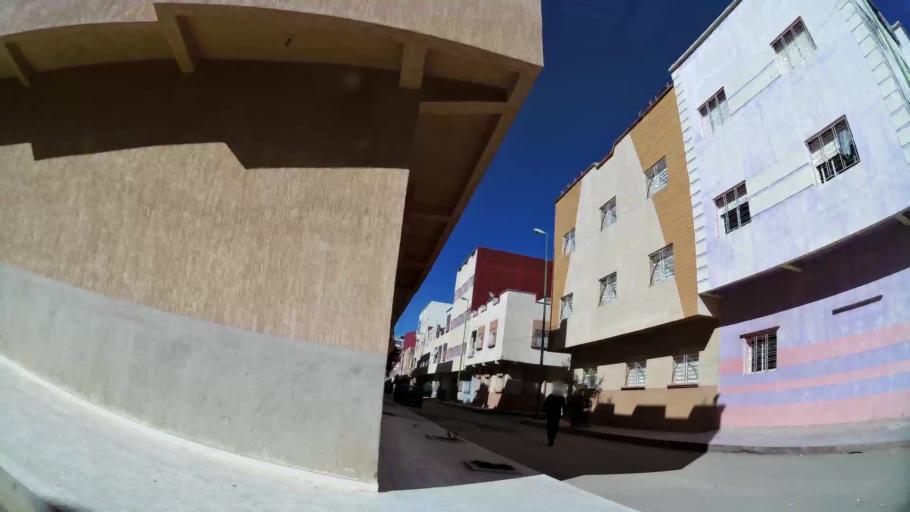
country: MA
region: Meknes-Tafilalet
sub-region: Meknes
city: Meknes
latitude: 33.8780
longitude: -5.5807
